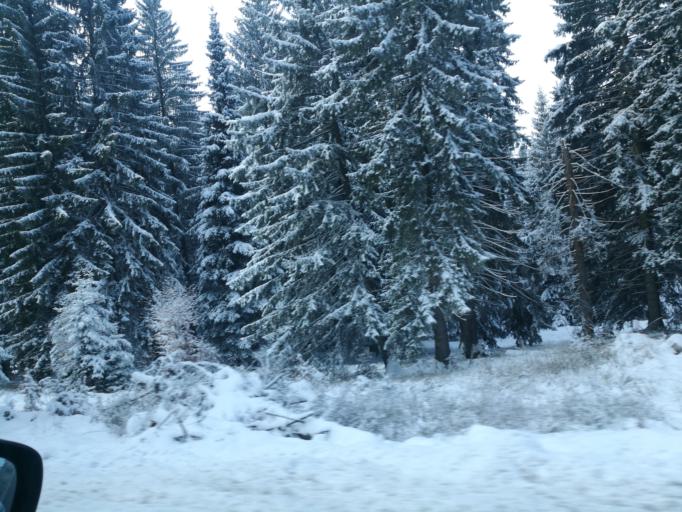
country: RO
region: Brasov
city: Brasov
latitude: 45.6137
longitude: 25.5466
